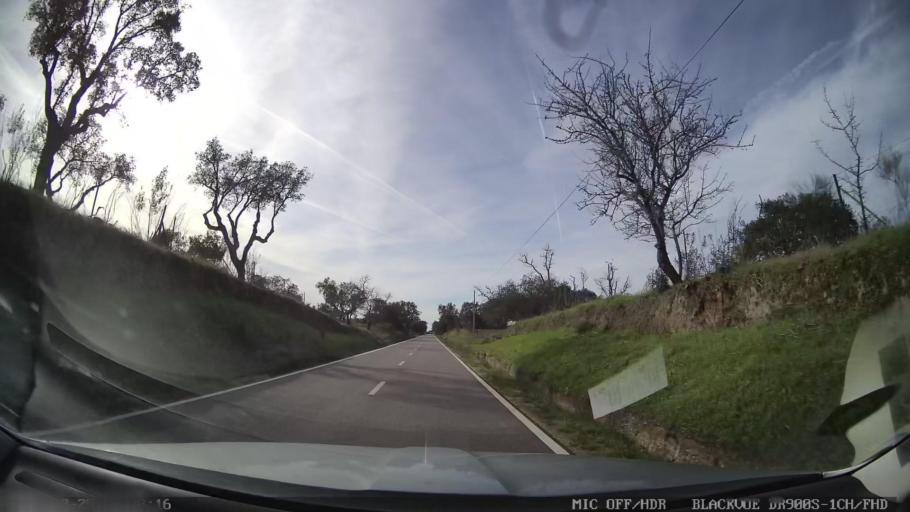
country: PT
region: Portalegre
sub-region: Nisa
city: Nisa
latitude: 39.4528
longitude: -7.7114
